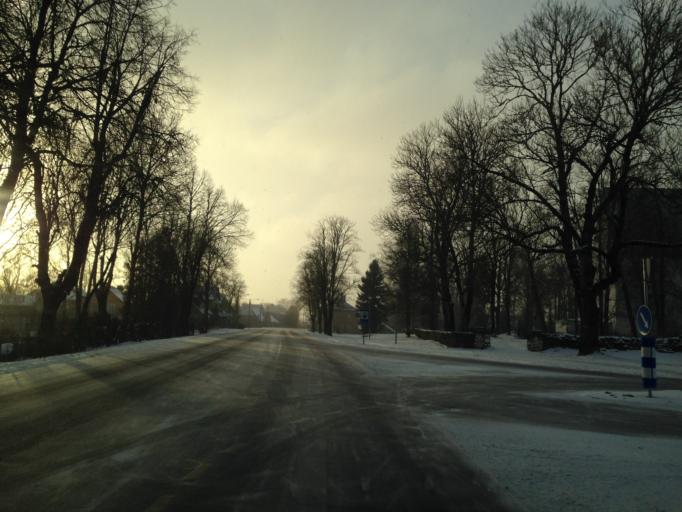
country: EE
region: Raplamaa
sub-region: Maerjamaa vald
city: Marjamaa
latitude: 58.9118
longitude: 24.4328
